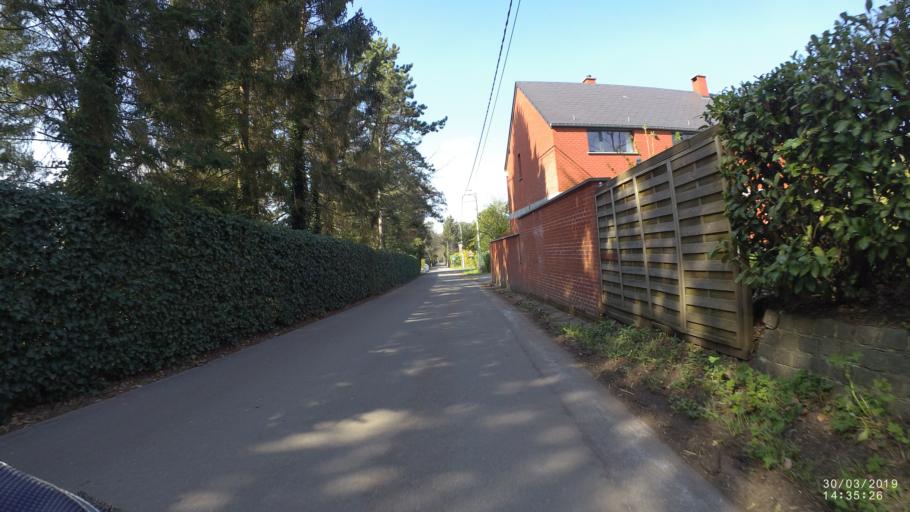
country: BE
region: Wallonia
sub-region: Province du Brabant Wallon
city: Rixensart
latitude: 50.7233
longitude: 4.5606
